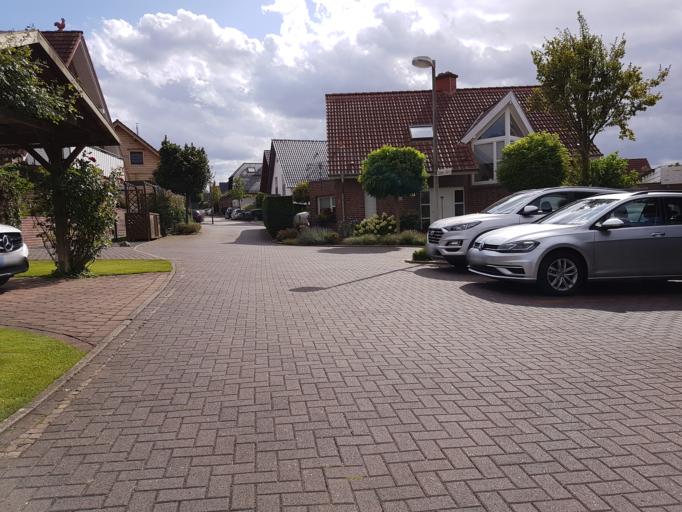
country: DE
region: North Rhine-Westphalia
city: Olfen
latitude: 51.7014
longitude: 7.3776
